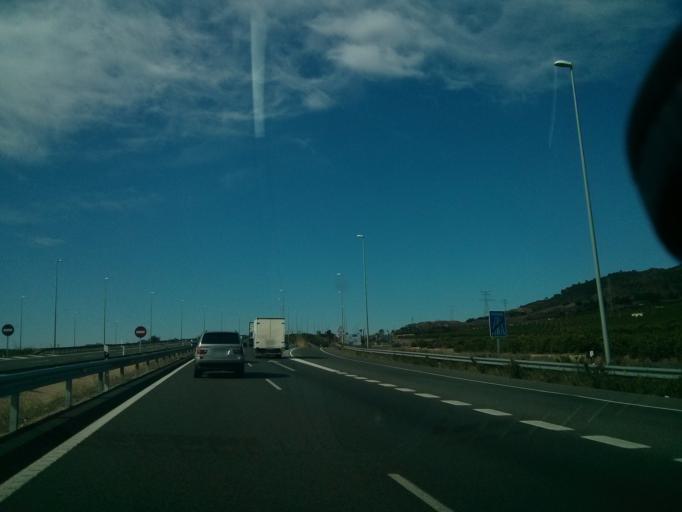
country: ES
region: Valencia
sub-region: Provincia de Valencia
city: Faura
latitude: 39.7063
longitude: -0.2580
